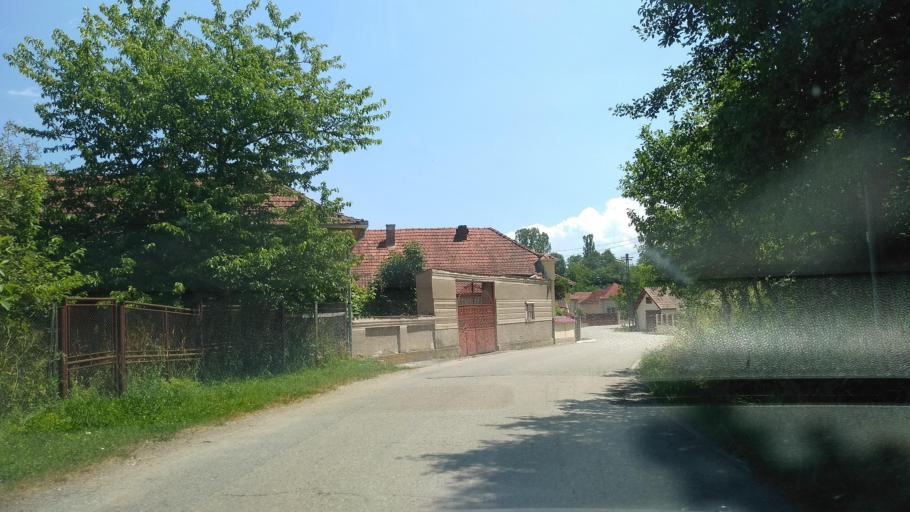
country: RO
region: Hunedoara
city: Densus
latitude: 45.5554
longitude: 22.8206
